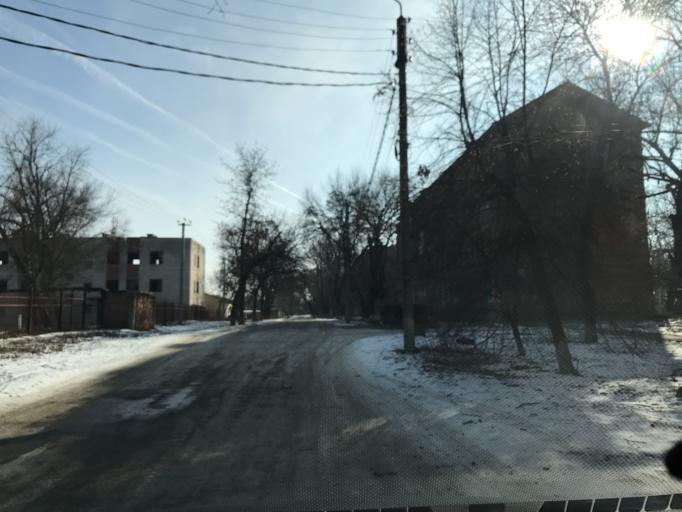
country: RU
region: Rostov
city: Kamensk-Shakhtinskiy
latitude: 48.3253
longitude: 40.2482
